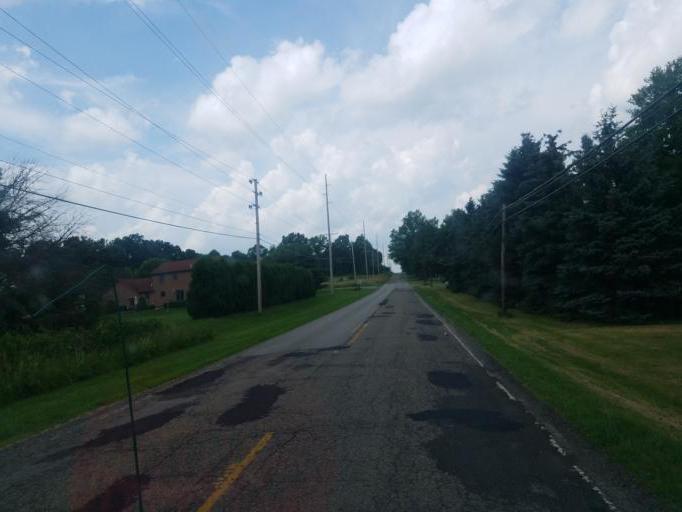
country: US
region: Ohio
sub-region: Mahoning County
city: Canfield
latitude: 40.9718
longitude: -80.7966
